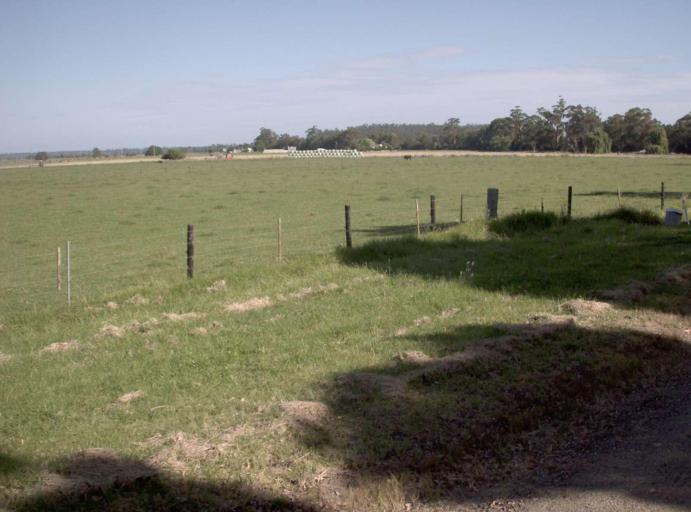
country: AU
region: Victoria
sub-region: East Gippsland
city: Lakes Entrance
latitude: -37.7351
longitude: 148.5049
